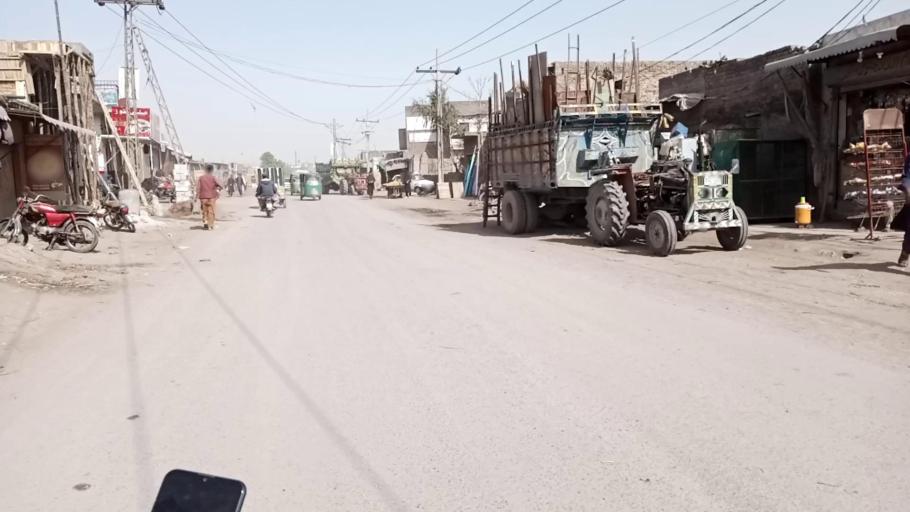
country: PK
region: Khyber Pakhtunkhwa
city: Peshawar
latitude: 33.9867
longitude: 71.6331
